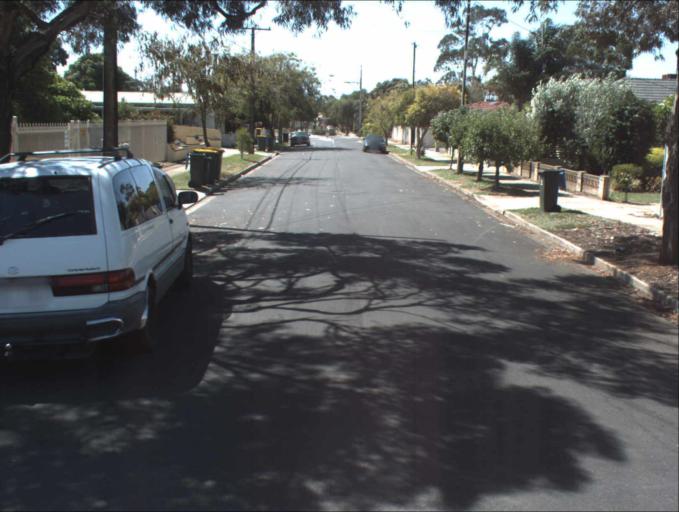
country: AU
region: South Australia
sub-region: Port Adelaide Enfield
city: Blair Athol
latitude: -34.8590
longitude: 138.5871
